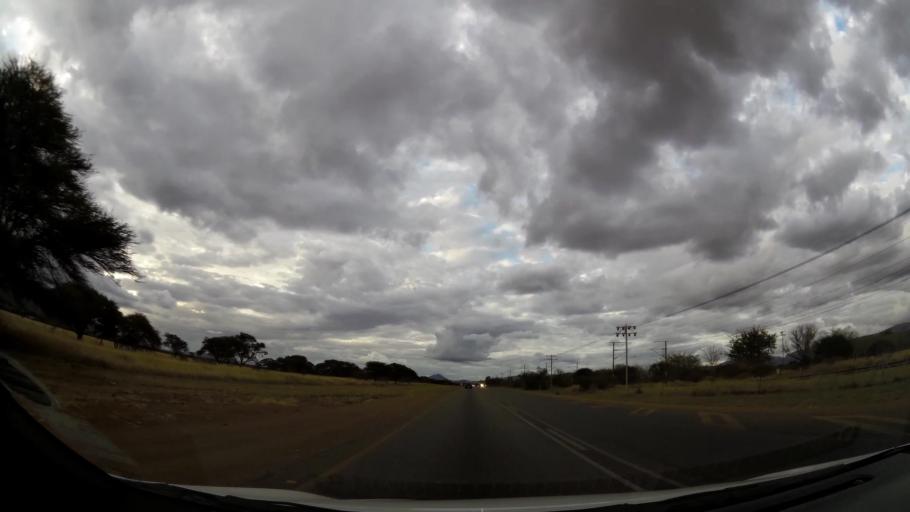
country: ZA
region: Limpopo
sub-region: Waterberg District Municipality
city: Mokopane
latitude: -24.2520
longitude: 28.9897
